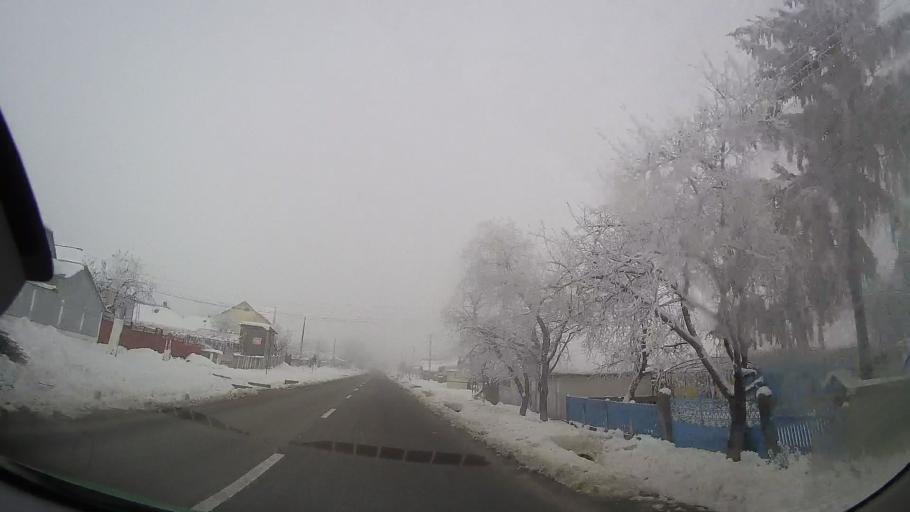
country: RO
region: Iasi
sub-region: Comuna Mircesti
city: Mircesti
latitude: 47.0964
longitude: 26.8193
